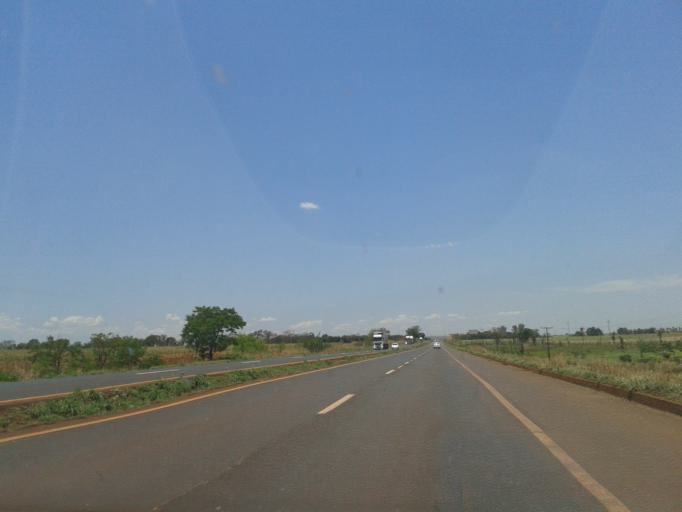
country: BR
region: Goias
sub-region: Itumbiara
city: Itumbiara
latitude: -18.4707
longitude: -49.1884
